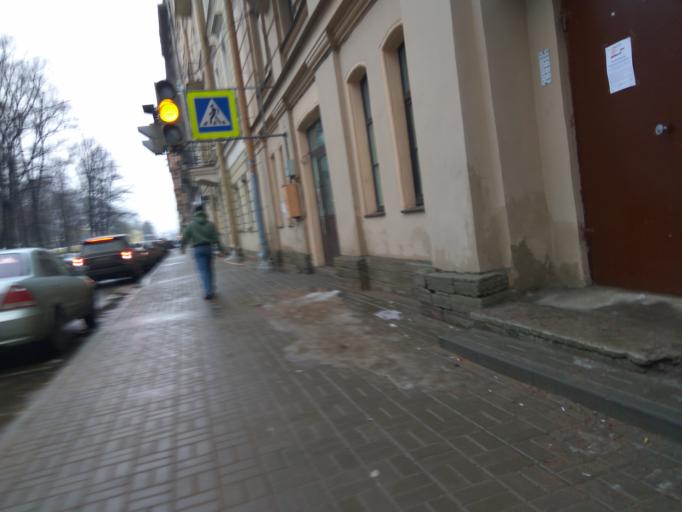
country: RU
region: St.-Petersburg
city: Centralniy
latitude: 59.9454
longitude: 30.3782
